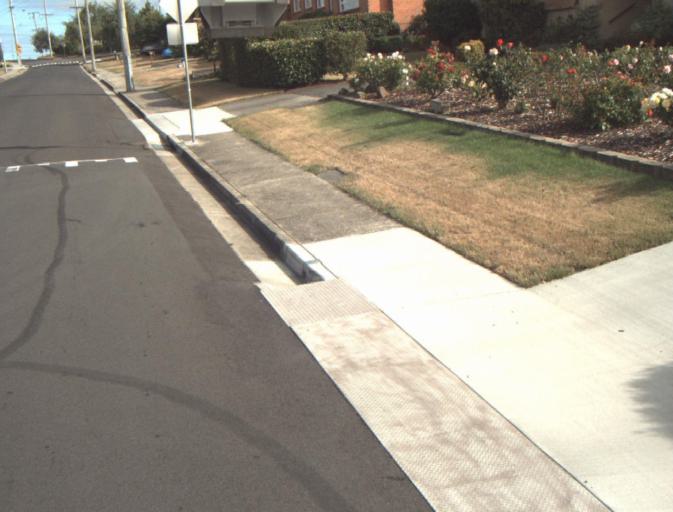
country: AU
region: Tasmania
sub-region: Launceston
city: Invermay
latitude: -41.3925
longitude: 147.1301
